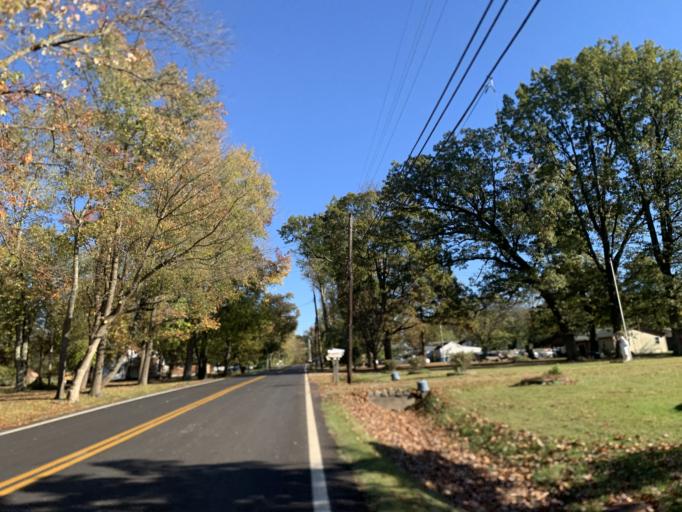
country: US
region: Kentucky
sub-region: Jefferson County
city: Pleasure Ridge Park
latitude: 38.1570
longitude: -85.8739
